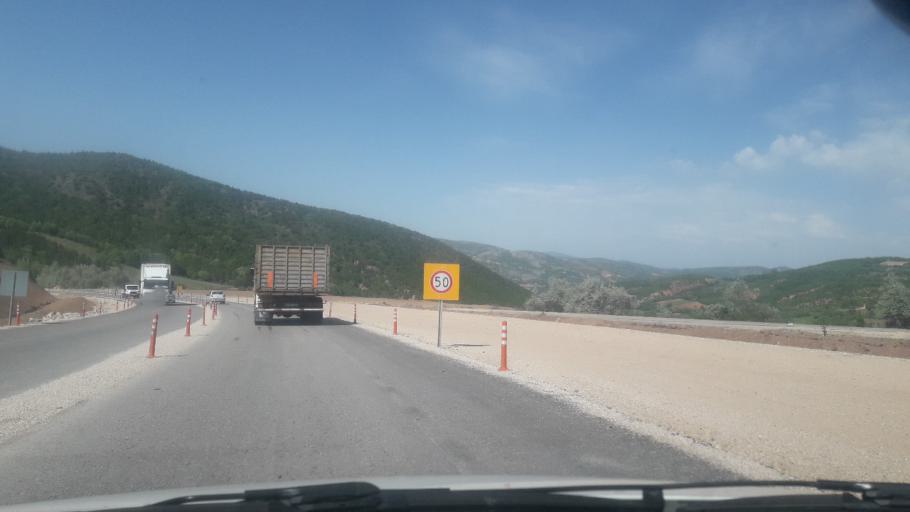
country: TR
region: Tokat
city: Tokat
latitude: 40.2082
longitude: 36.4996
